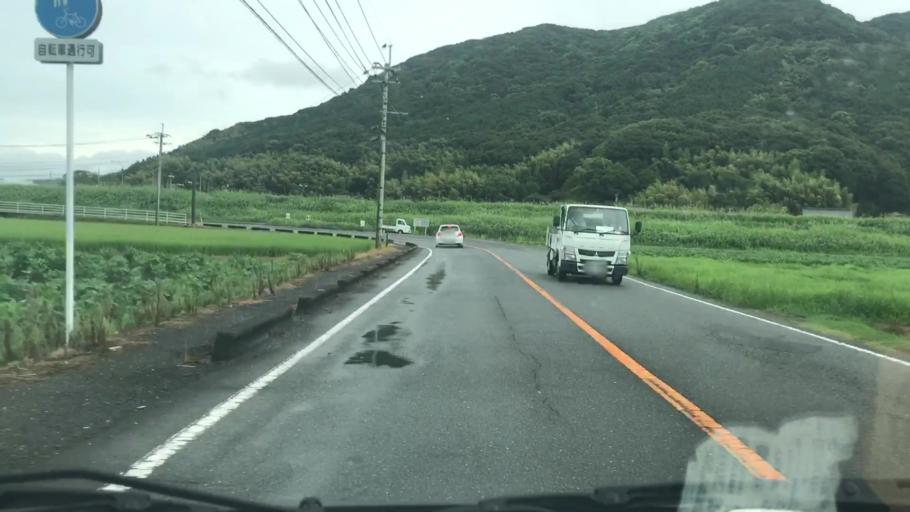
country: JP
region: Saga Prefecture
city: Takeocho-takeo
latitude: 33.2001
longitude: 130.0520
